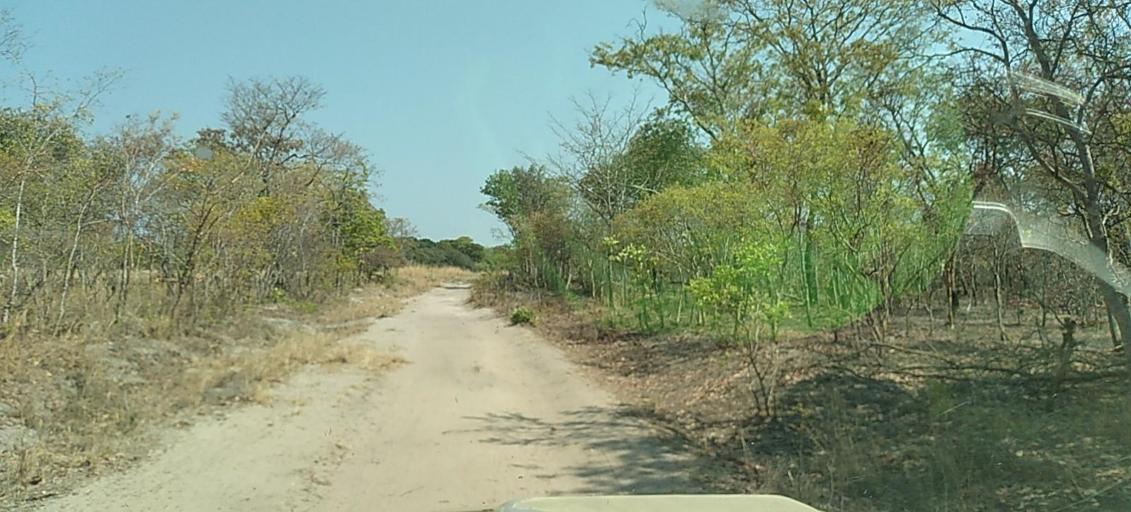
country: ZM
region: North-Western
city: Kalengwa
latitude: -13.2964
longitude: 24.7909
